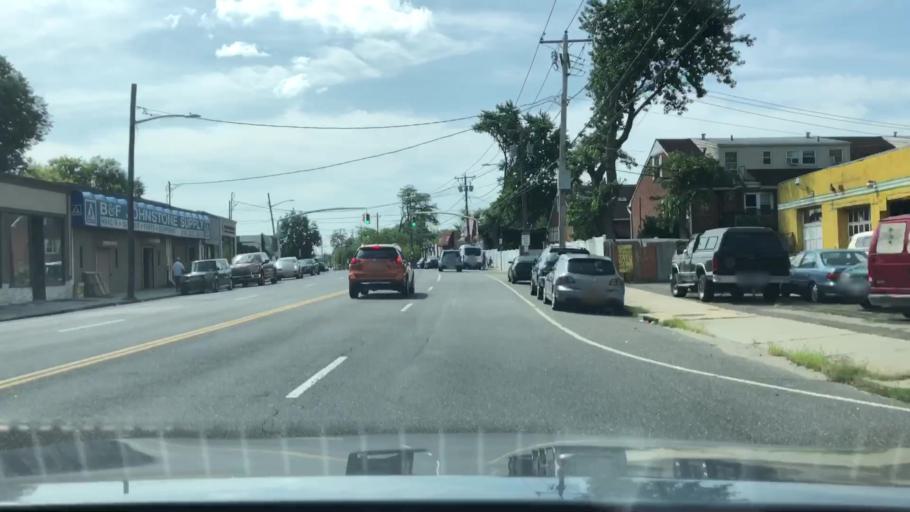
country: US
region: New York
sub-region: Nassau County
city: South Hempstead
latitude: 40.6716
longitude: -73.6109
